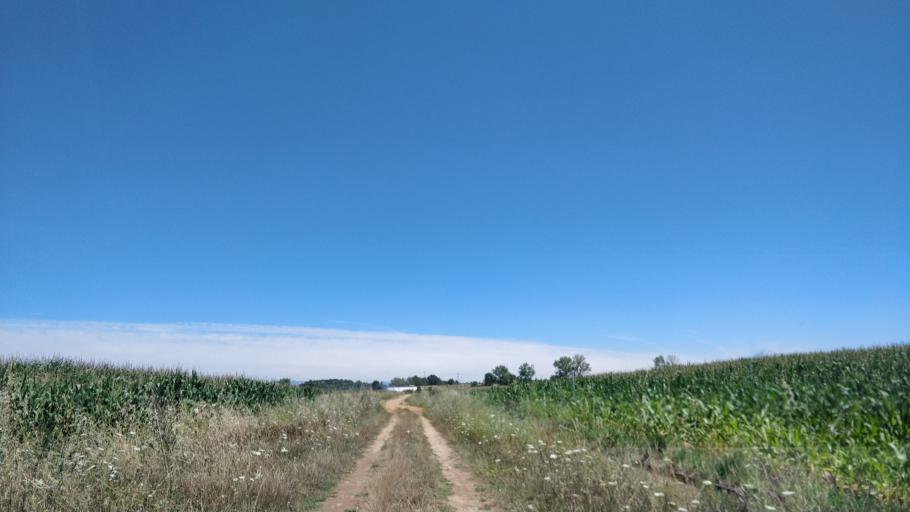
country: ES
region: Castille and Leon
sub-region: Provincia de Leon
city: Bustillo del Paramo
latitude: 42.4711
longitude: -5.8129
